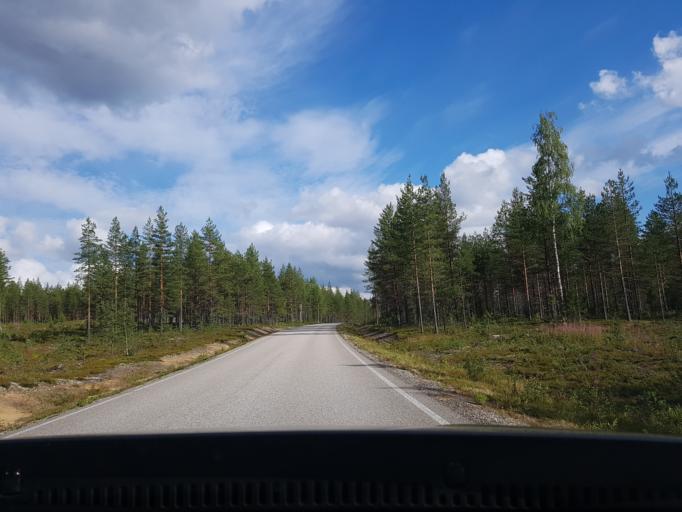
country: FI
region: Kainuu
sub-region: Kehys-Kainuu
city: Kuhmo
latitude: 64.6196
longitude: 29.7062
